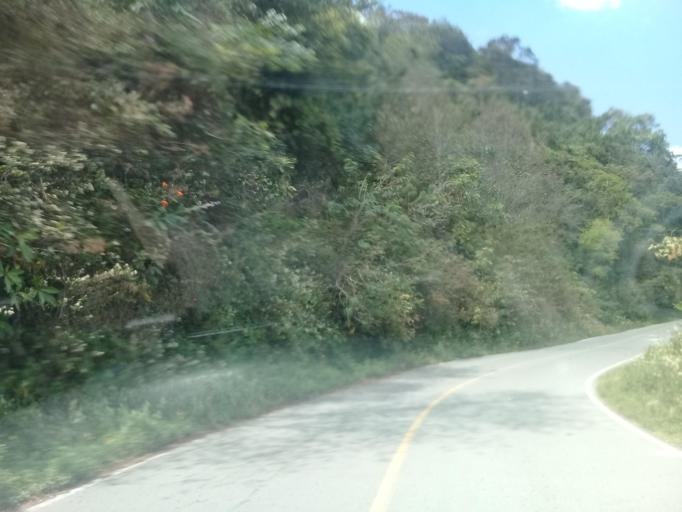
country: MX
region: Veracruz
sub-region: Tlilapan
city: Tonalixco
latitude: 18.7891
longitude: -97.0577
